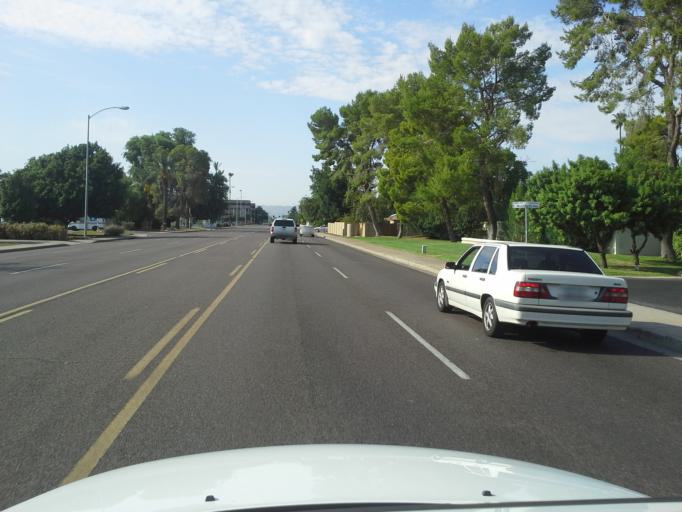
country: US
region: Arizona
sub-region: Maricopa County
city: Phoenix
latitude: 33.5209
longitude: -112.0476
